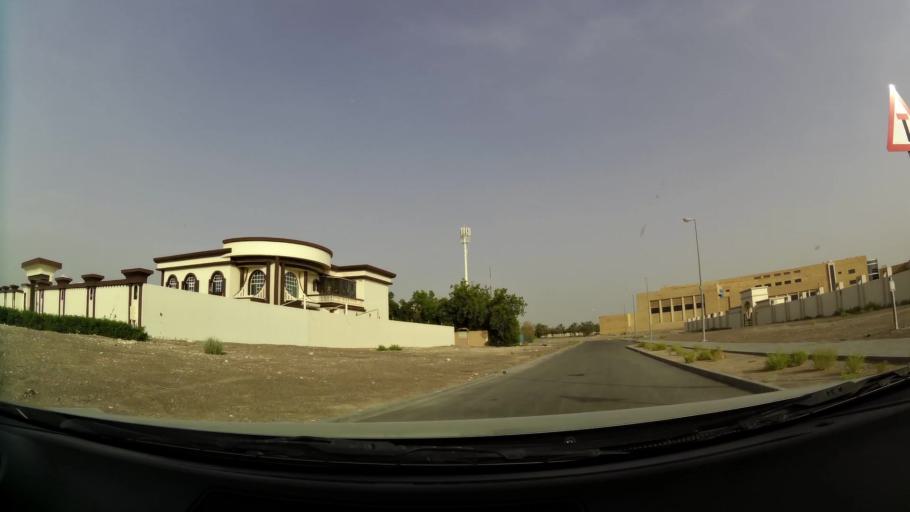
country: AE
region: Abu Dhabi
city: Al Ain
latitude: 24.2154
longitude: 55.6672
